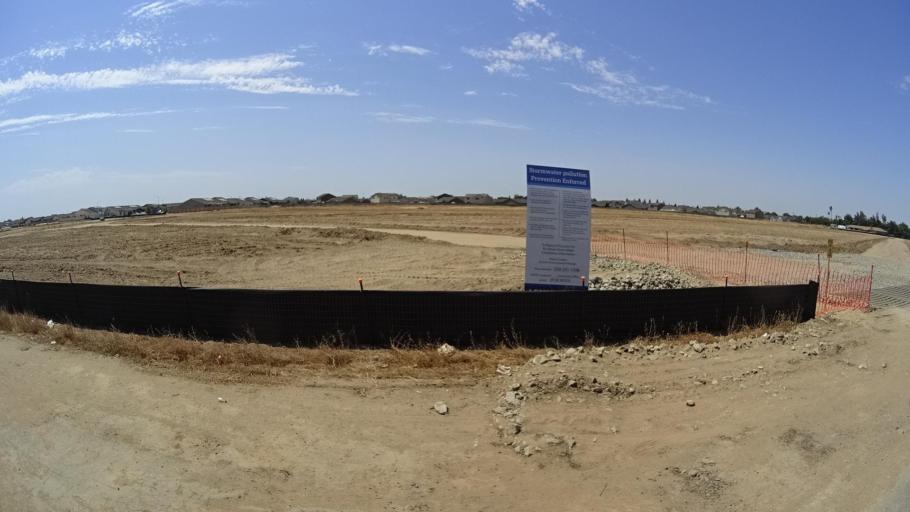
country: US
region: California
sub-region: Fresno County
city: Tarpey Village
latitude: 36.7867
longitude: -119.6785
